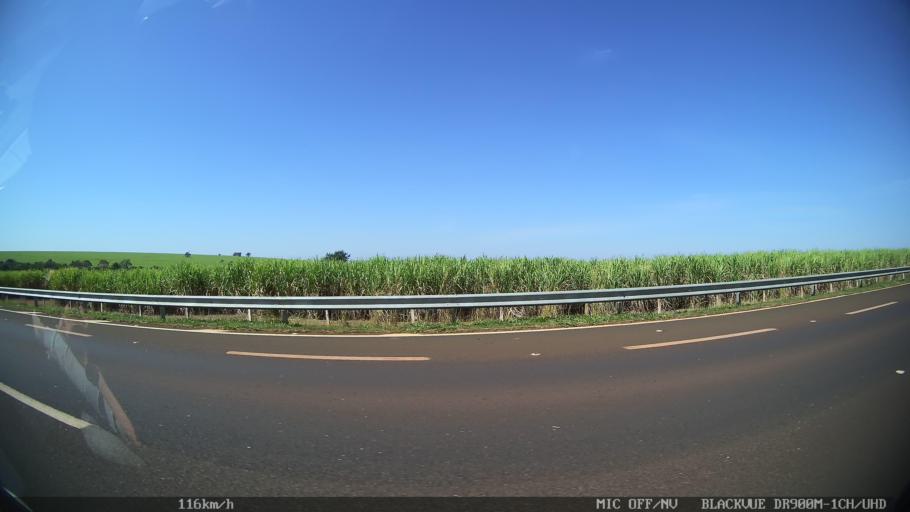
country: BR
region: Sao Paulo
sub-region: Batatais
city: Batatais
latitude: -20.8258
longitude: -47.5939
